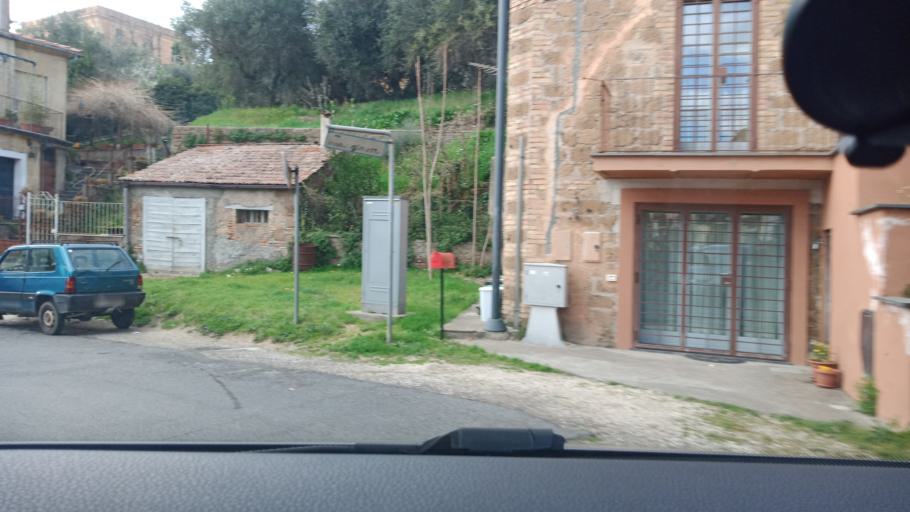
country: IT
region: Latium
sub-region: Provincia di Rieti
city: Stimigliano
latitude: 42.2995
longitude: 12.5650
